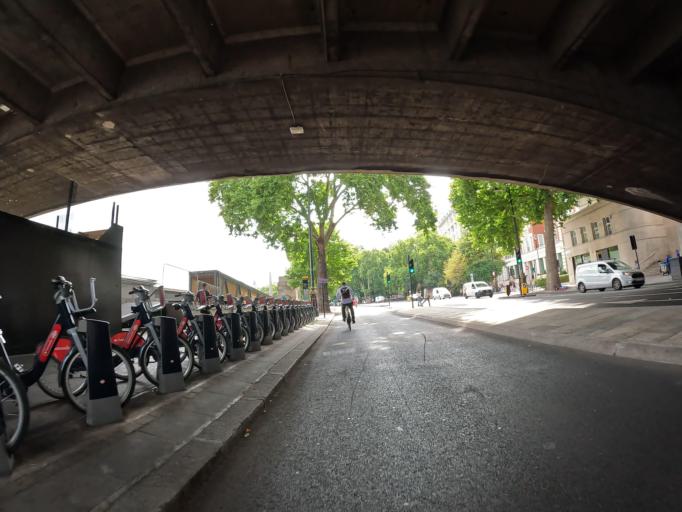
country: GB
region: England
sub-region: Greater London
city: Bethnal Green
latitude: 51.4978
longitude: -0.0622
